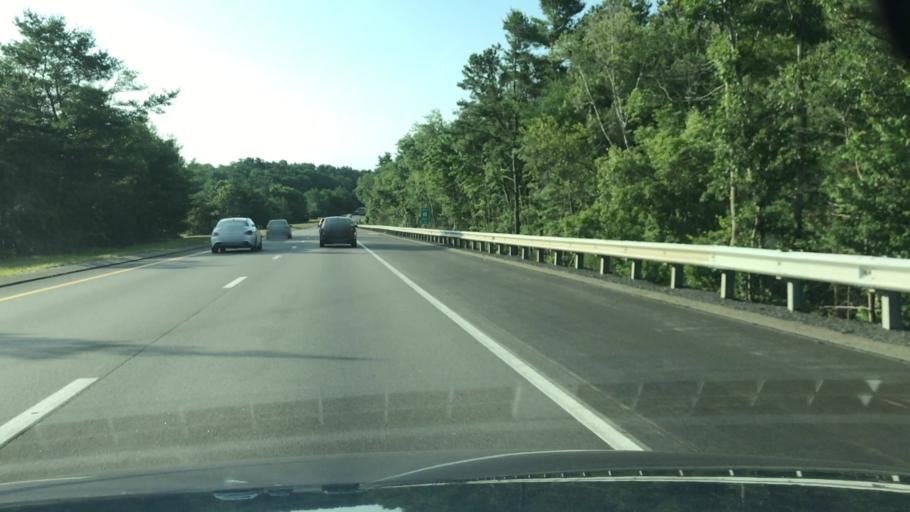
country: US
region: Massachusetts
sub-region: Plymouth County
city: Plymouth
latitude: 41.9229
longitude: -70.6277
